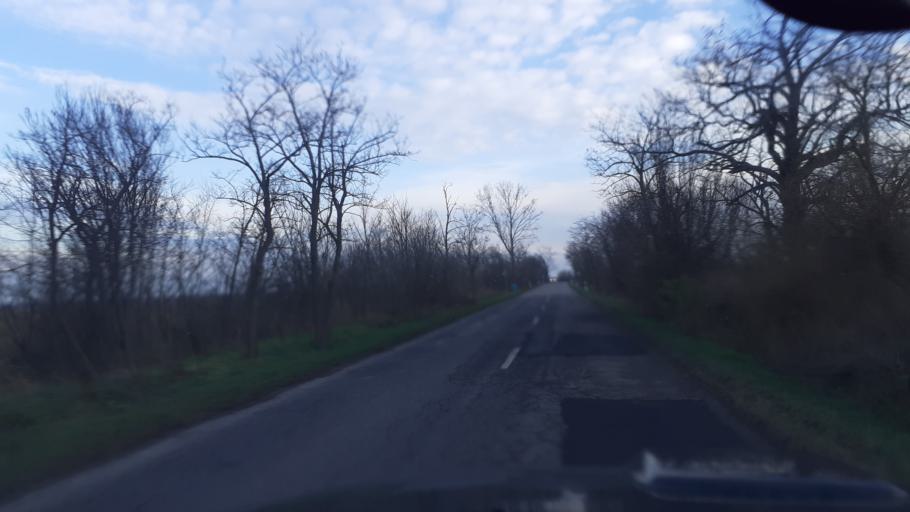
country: HU
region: Bacs-Kiskun
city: Kunszentmiklos
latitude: 46.9732
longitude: 19.1455
